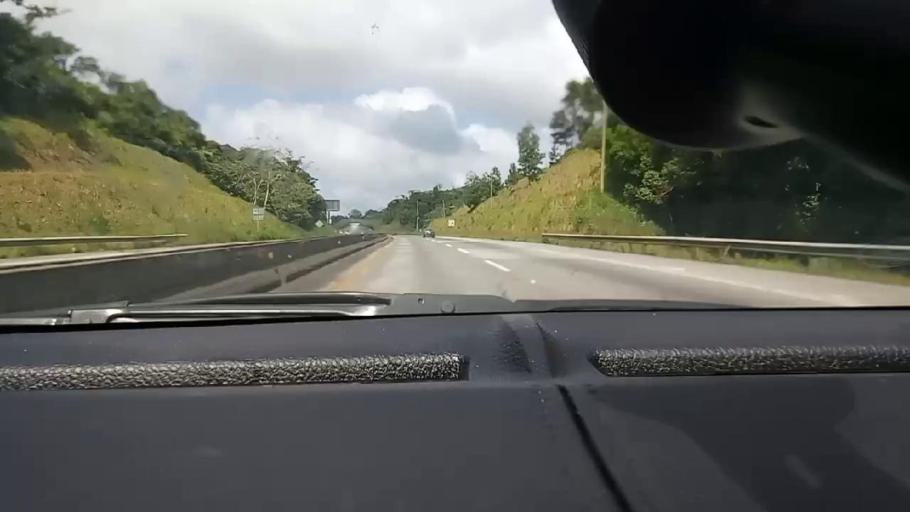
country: PA
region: Colon
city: Rio Rita
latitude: 9.2952
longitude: -79.7849
